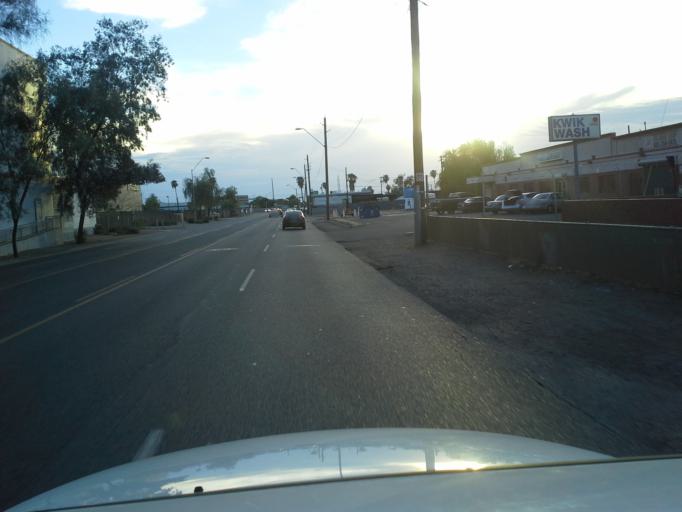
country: US
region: Arizona
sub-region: Maricopa County
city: Phoenix
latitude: 33.4369
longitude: -112.0703
